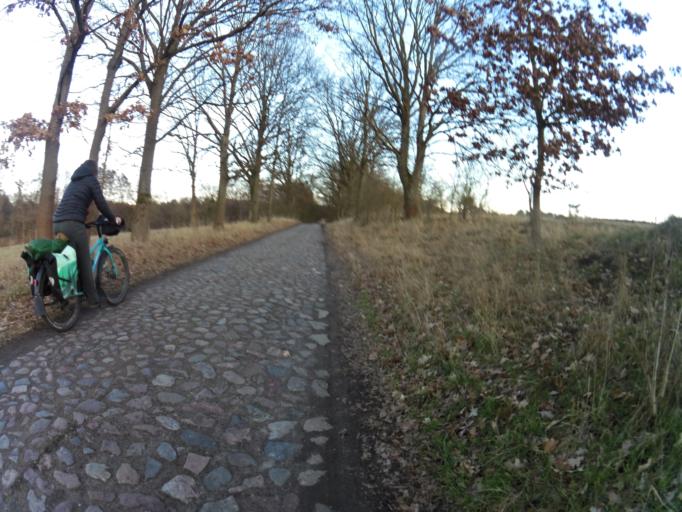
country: PL
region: West Pomeranian Voivodeship
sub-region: Powiat mysliborski
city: Debno
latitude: 52.8103
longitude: 14.7876
